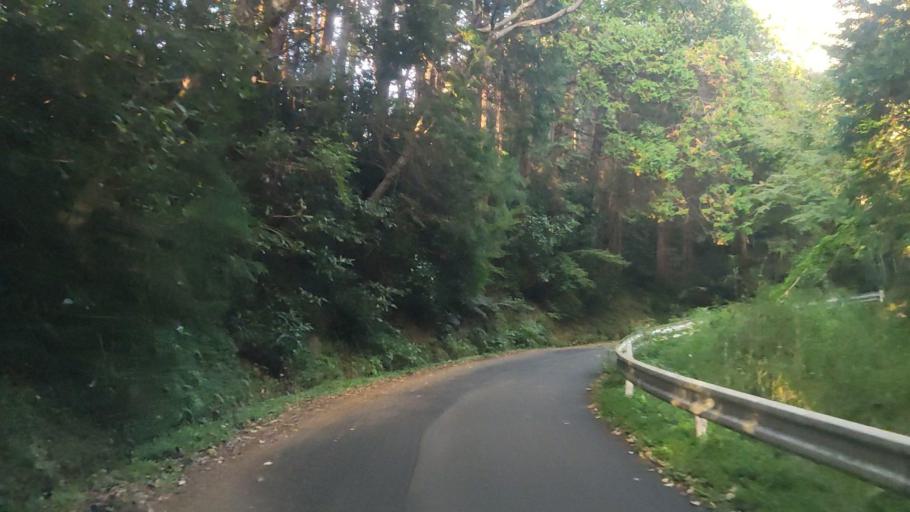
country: JP
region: Kanagawa
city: Hakone
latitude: 35.1329
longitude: 138.9945
